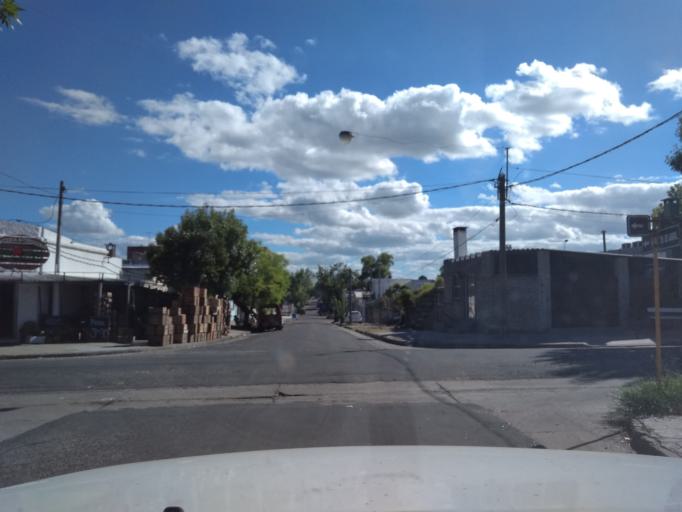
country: UY
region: Florida
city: Florida
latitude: -34.1014
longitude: -56.2086
